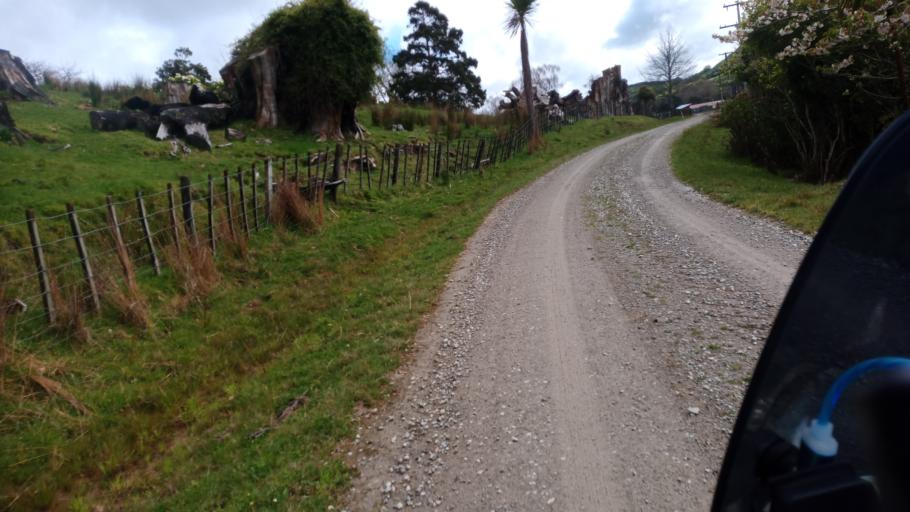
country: NZ
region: Gisborne
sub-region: Gisborne District
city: Gisborne
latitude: -38.5441
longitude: 178.1283
